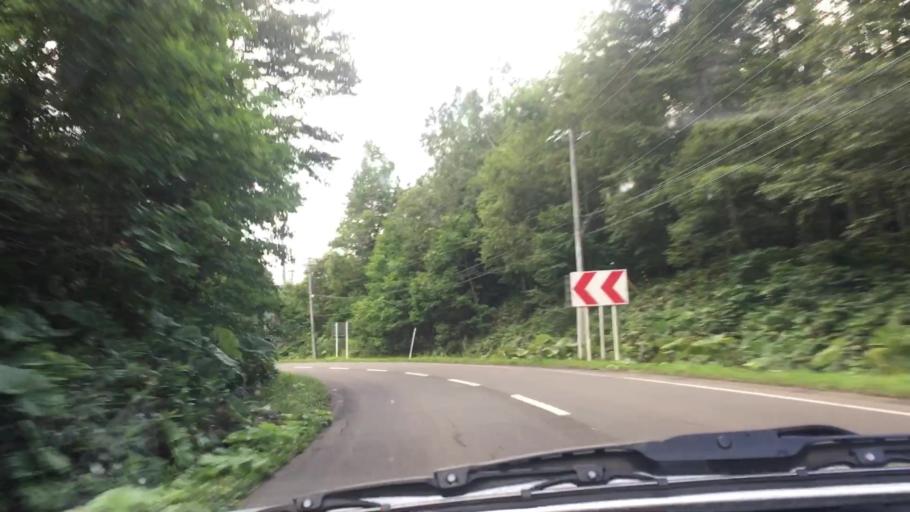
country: JP
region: Hokkaido
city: Shimo-furano
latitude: 43.1005
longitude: 142.6847
